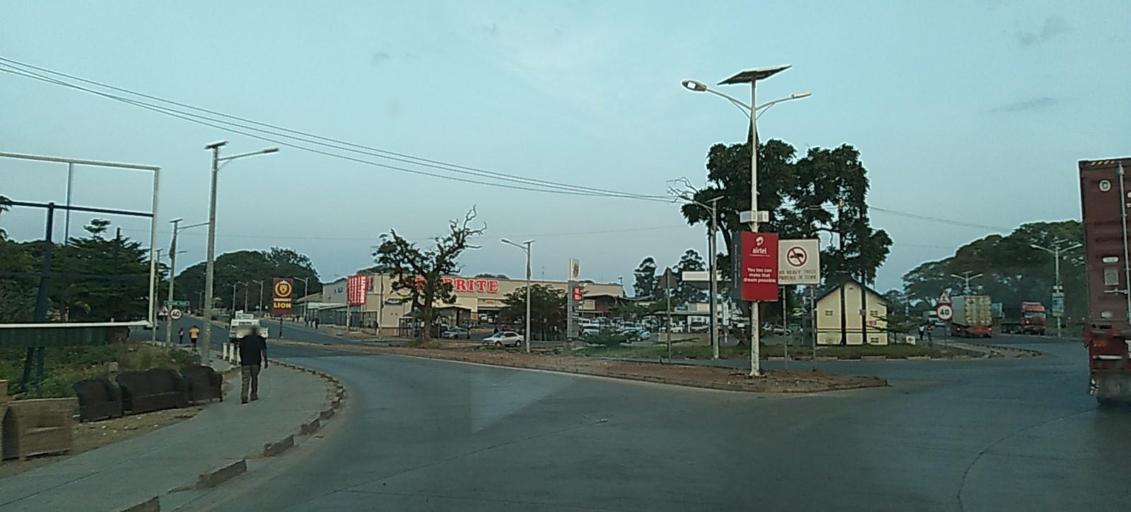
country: ZM
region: Copperbelt
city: Chingola
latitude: -12.5480
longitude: 27.8575
